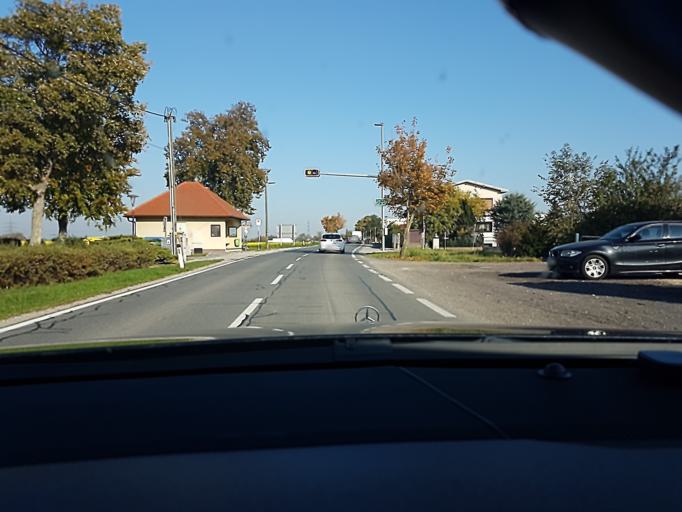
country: AT
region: Lower Austria
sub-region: Politischer Bezirk Modling
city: Achau
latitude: 48.0827
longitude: 16.3934
